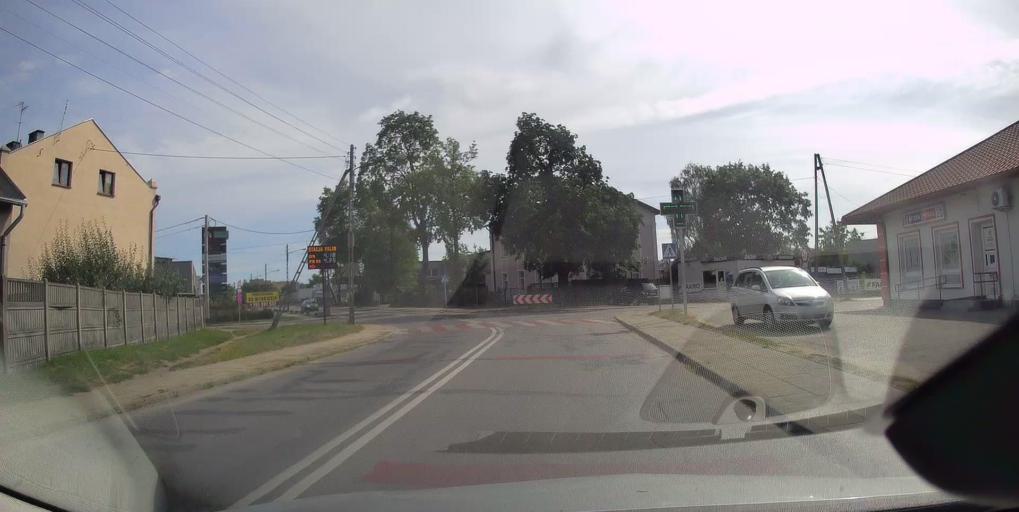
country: PL
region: Lodz Voivodeship
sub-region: Powiat tomaszowski
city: Tomaszow Mazowiecki
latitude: 51.5350
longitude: 19.9962
